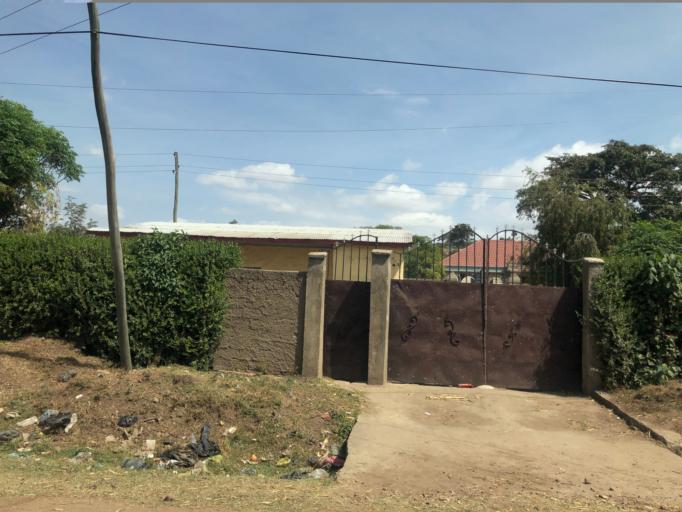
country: ET
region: Oromiya
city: Shashemene
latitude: 7.2847
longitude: 38.6516
